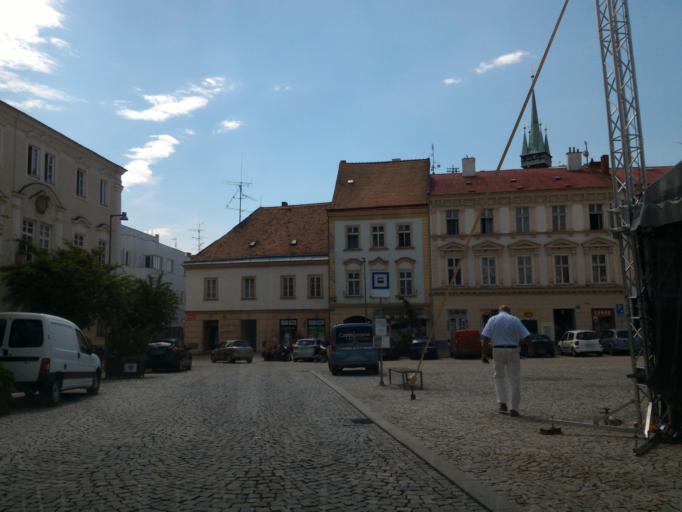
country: CZ
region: South Moravian
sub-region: Okres Znojmo
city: Znojmo
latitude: 48.8567
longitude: 16.0487
